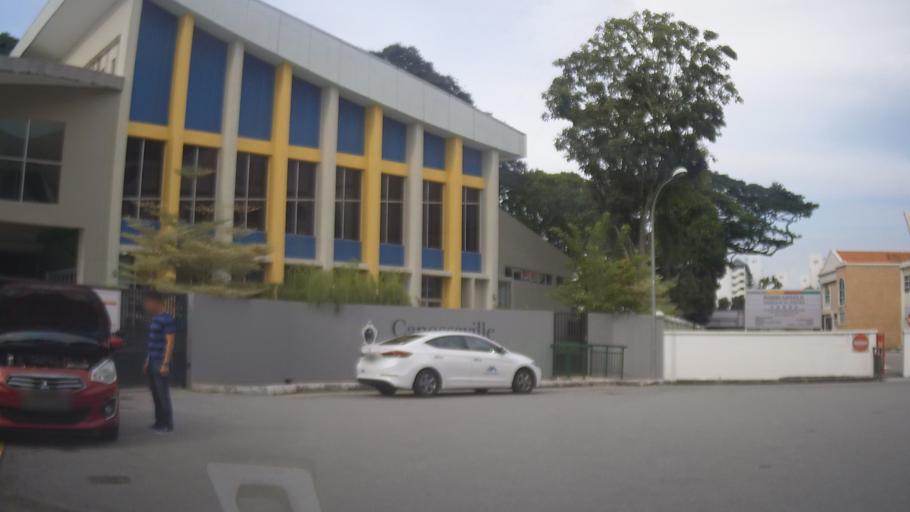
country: SG
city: Singapore
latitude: 1.3261
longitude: 103.8826
